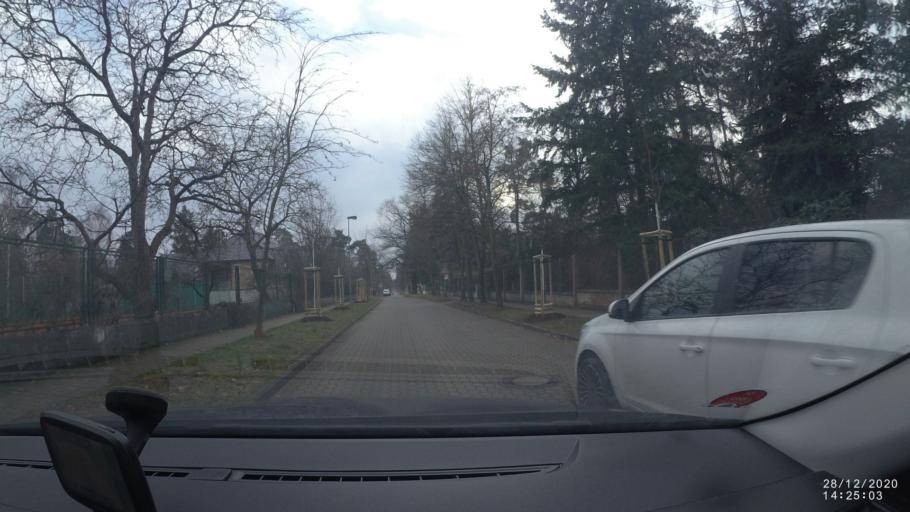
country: CZ
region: Central Bohemia
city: Sestajovice
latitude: 50.0954
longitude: 14.6669
